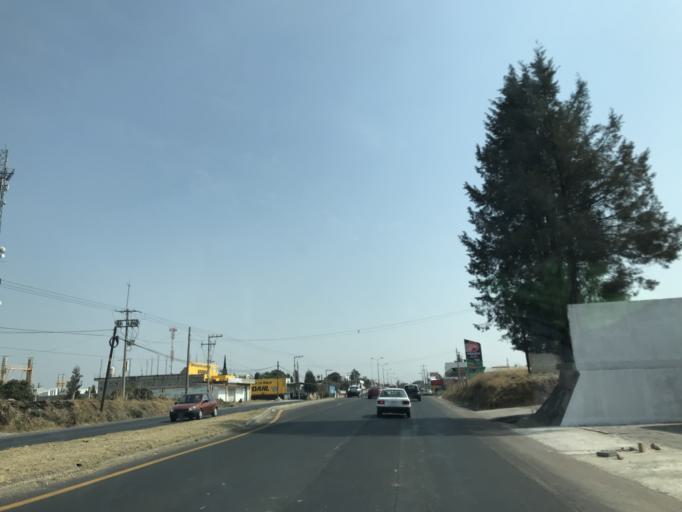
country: MX
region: Tlaxcala
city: Xiloxoxtla
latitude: 19.2644
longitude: -98.1991
